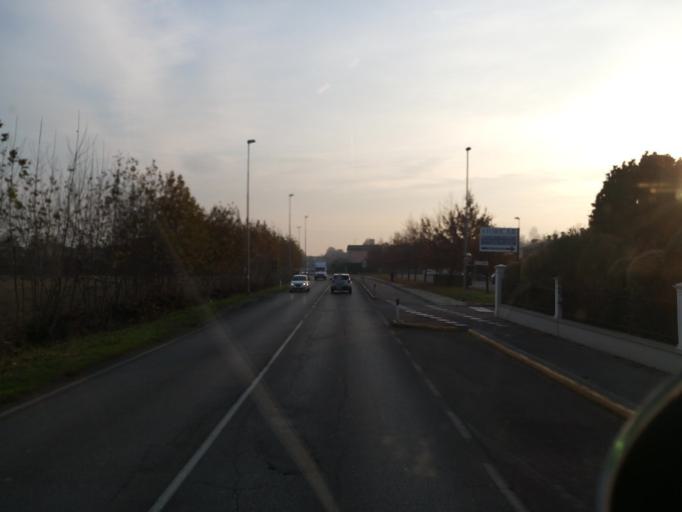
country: IT
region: Lombardy
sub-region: Provincia di Brescia
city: Poncarale
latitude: 45.4661
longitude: 10.1744
